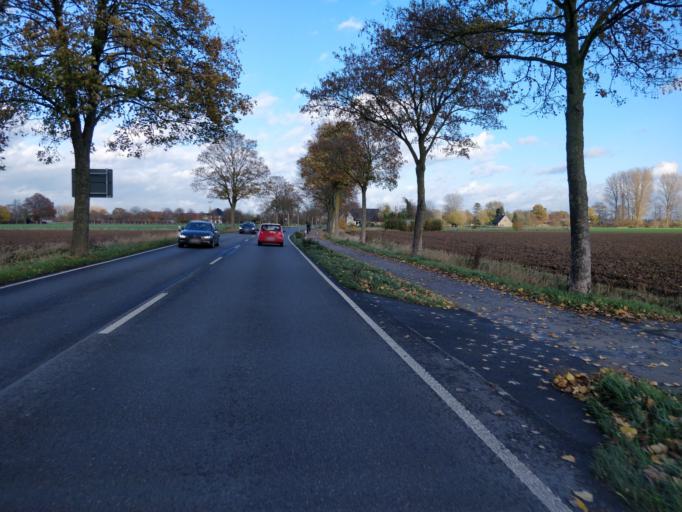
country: DE
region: North Rhine-Westphalia
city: Rees
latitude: 51.7730
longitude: 6.4162
